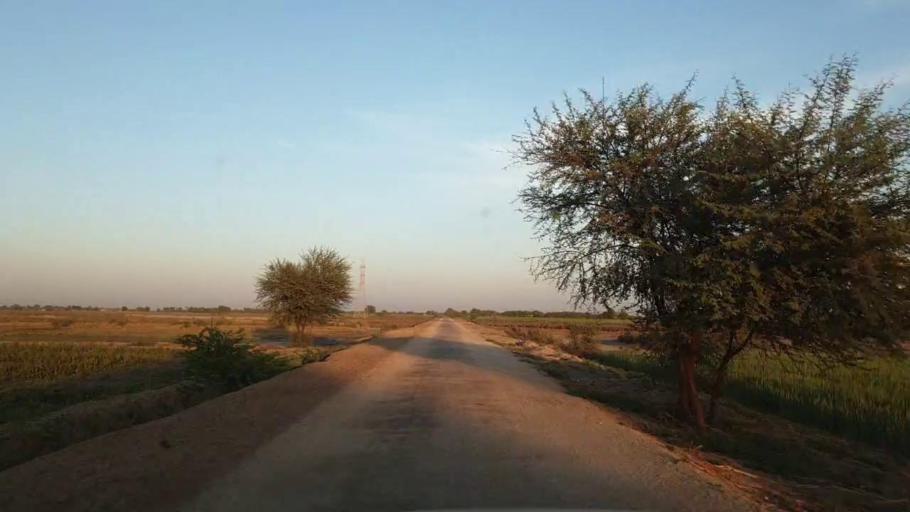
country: PK
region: Sindh
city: Kunri
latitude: 25.1375
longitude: 69.4365
